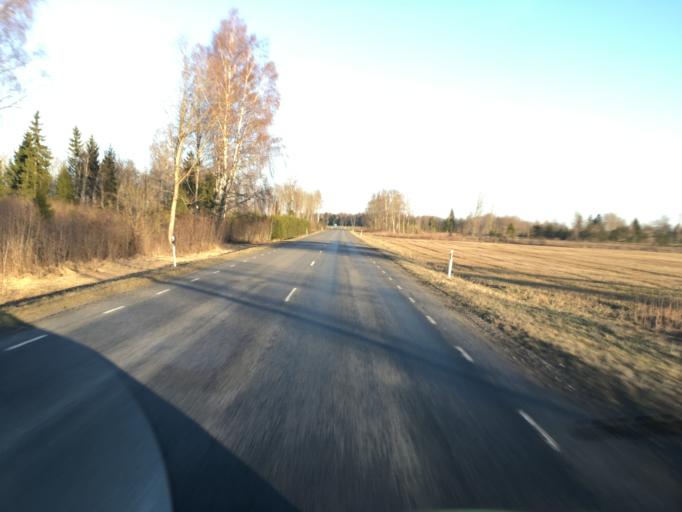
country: EE
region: Raplamaa
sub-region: Kehtna vald
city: Kehtna
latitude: 59.0609
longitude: 24.9369
